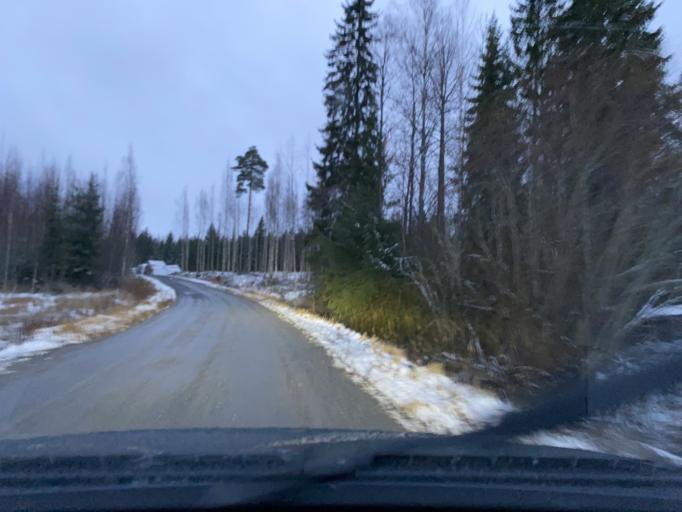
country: FI
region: Pirkanmaa
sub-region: Lounais-Pirkanmaa
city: Punkalaidun
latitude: 61.1589
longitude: 22.9598
